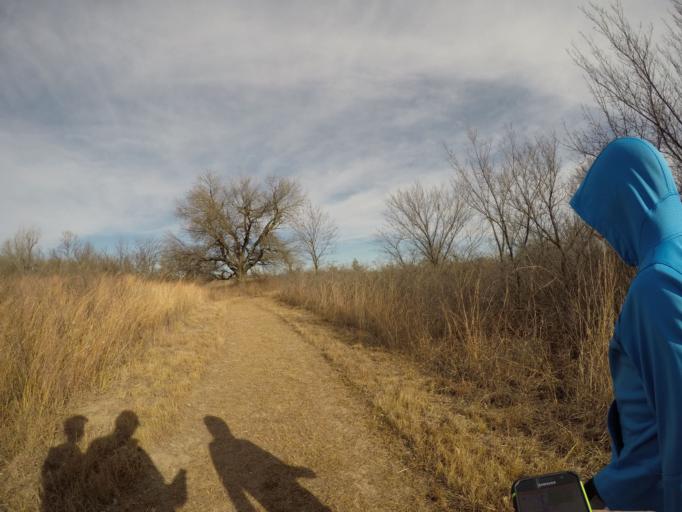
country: US
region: Kansas
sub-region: Reno County
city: Buhler
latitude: 38.1222
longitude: -97.8564
